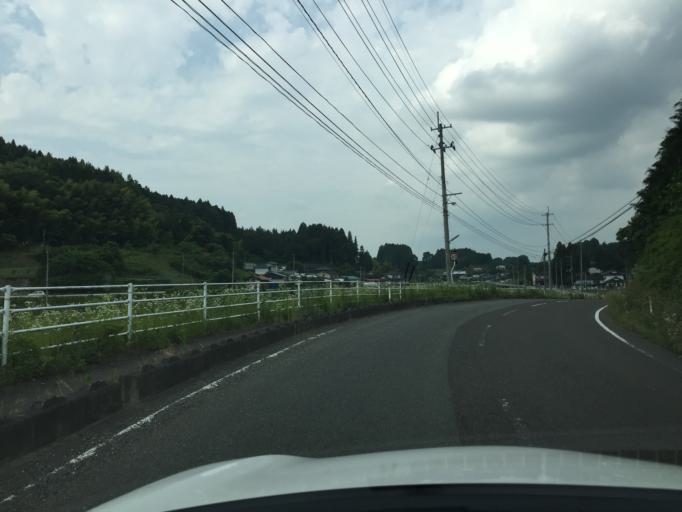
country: JP
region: Fukushima
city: Ishikawa
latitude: 37.2155
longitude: 140.4469
